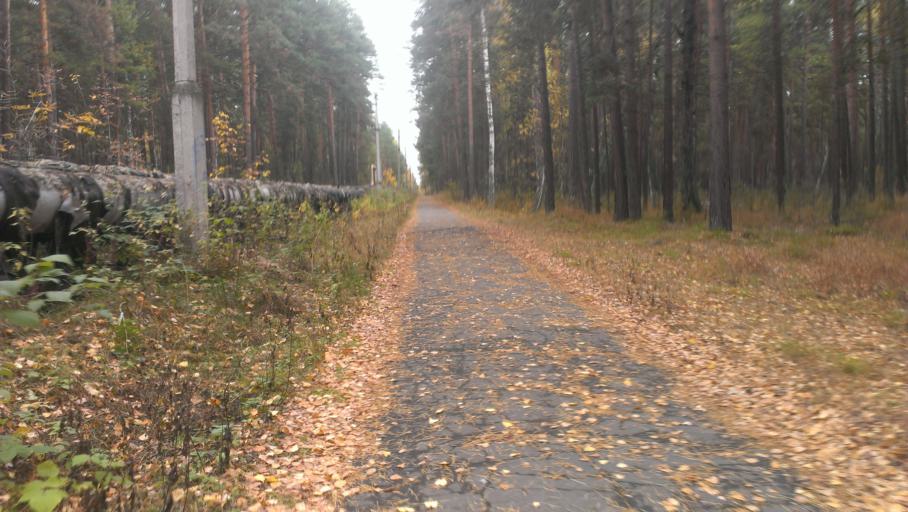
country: RU
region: Altai Krai
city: Yuzhnyy
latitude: 53.2673
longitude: 83.6832
